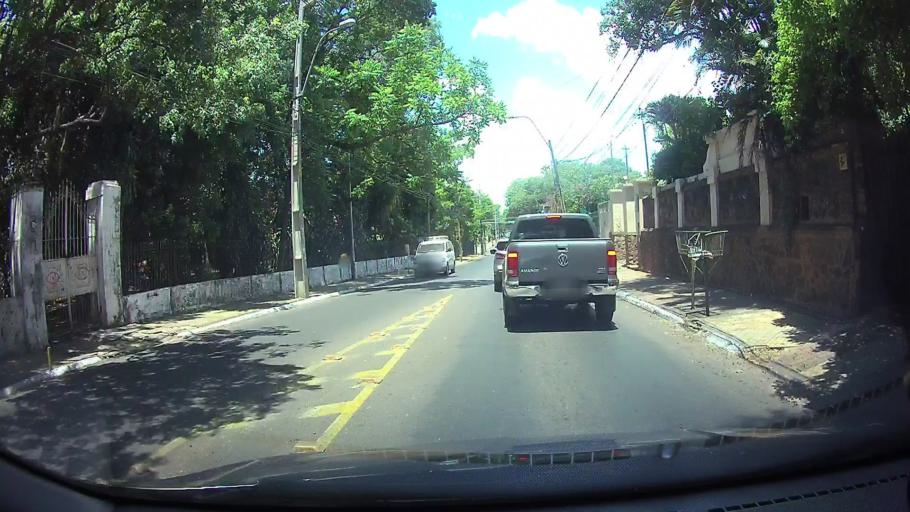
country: PY
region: Asuncion
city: Asuncion
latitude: -25.2873
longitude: -57.6109
